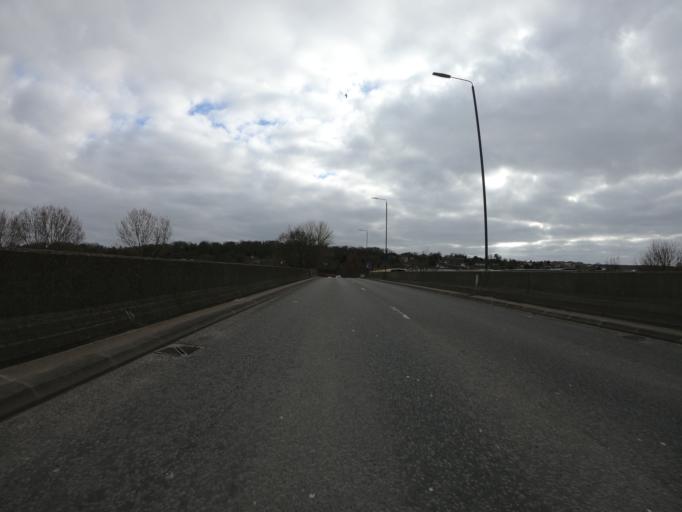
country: GB
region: England
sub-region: Greater London
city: Belvedere
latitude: 51.4924
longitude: 0.1562
